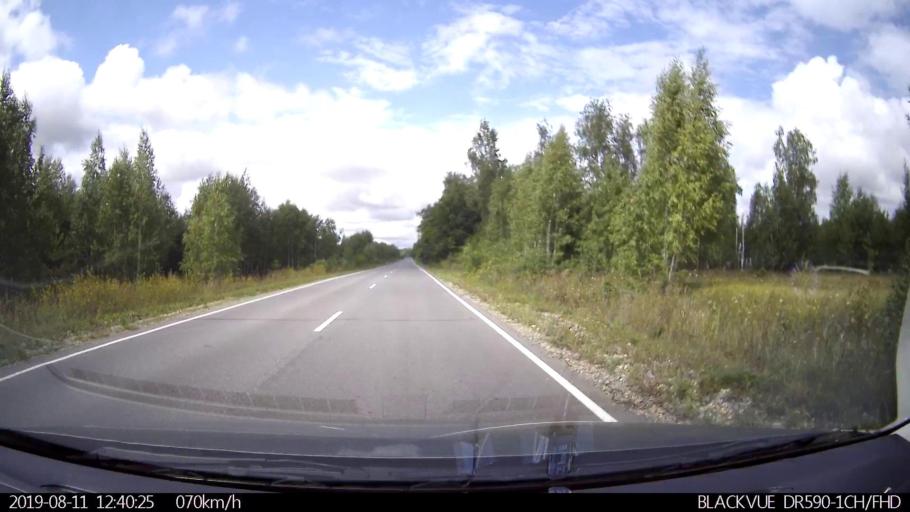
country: RU
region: Ulyanovsk
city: Ignatovka
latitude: 53.8385
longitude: 47.7812
